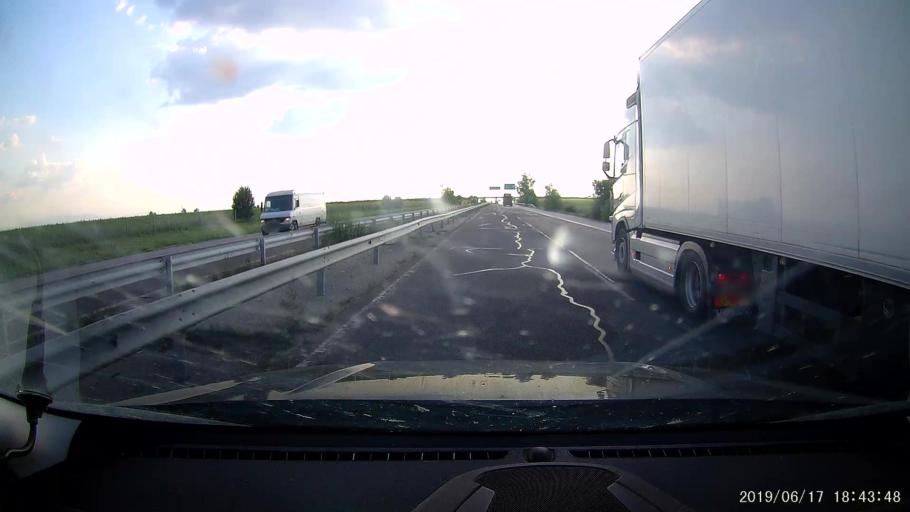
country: BG
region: Stara Zagora
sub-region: Obshtina Chirpan
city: Chirpan
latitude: 42.1922
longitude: 25.2023
